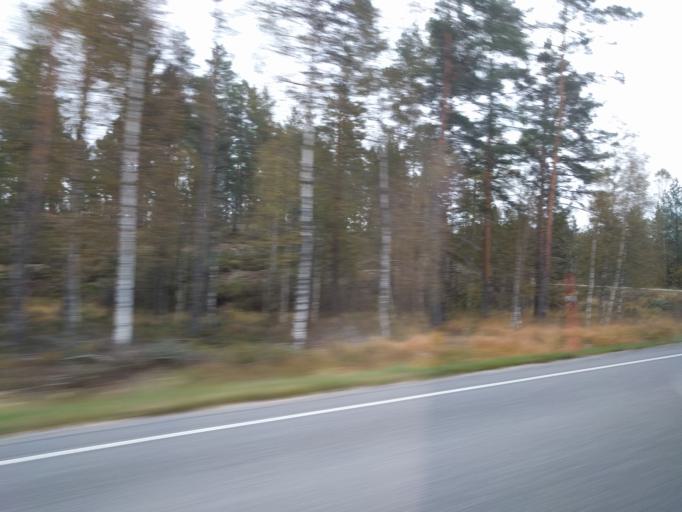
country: NO
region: Aust-Agder
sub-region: Evje og Hornnes
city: Evje
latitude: 58.5367
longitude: 7.7777
